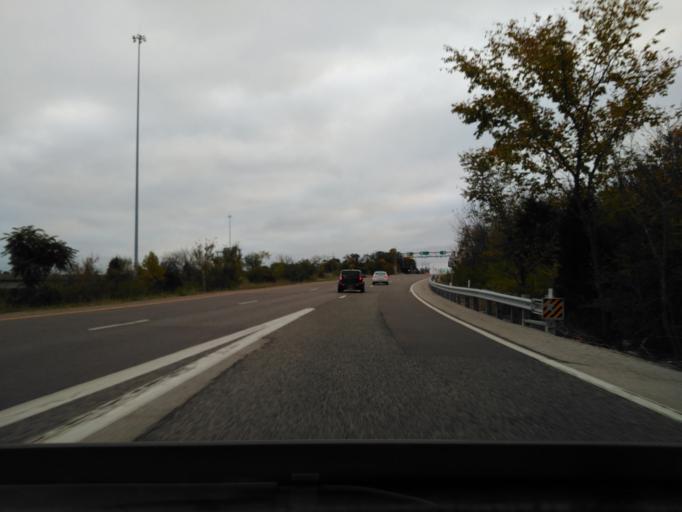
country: US
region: Missouri
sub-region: Saint Louis County
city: Sunset Hills
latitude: 38.5525
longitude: -90.4203
